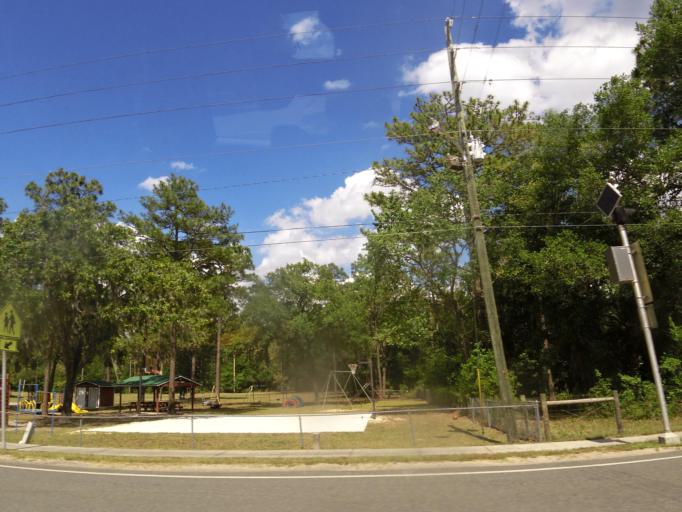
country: US
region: Florida
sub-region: Clay County
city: Keystone Heights
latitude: 29.8168
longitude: -81.9223
